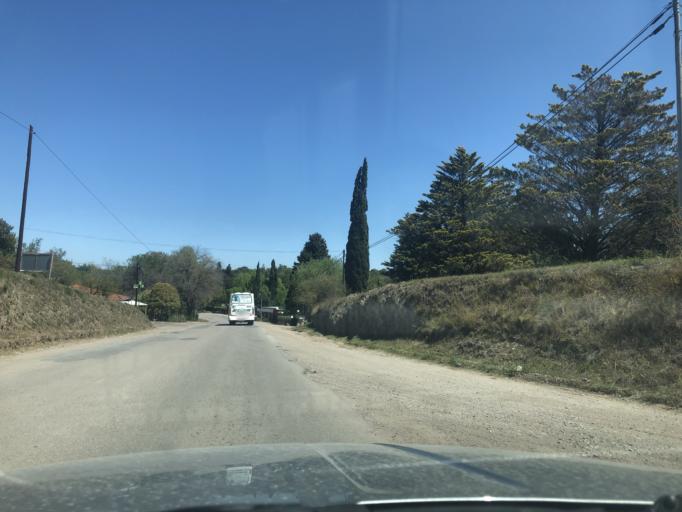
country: AR
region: Cordoba
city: La Granja
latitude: -31.0178
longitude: -64.2733
